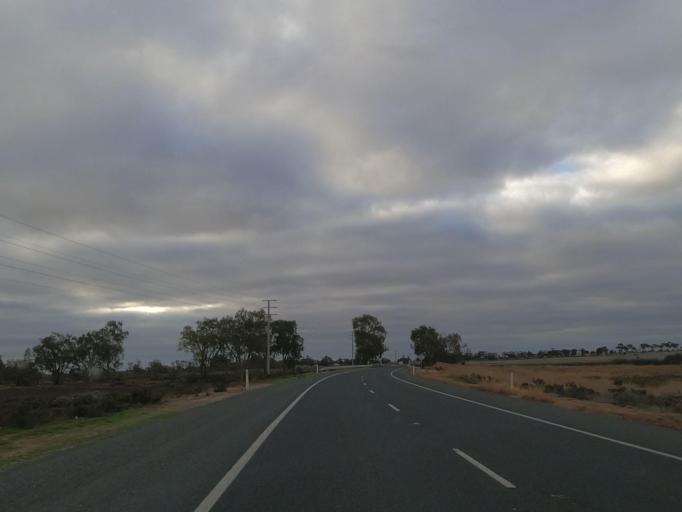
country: AU
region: Victoria
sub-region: Swan Hill
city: Swan Hill
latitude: -35.6205
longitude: 143.8035
